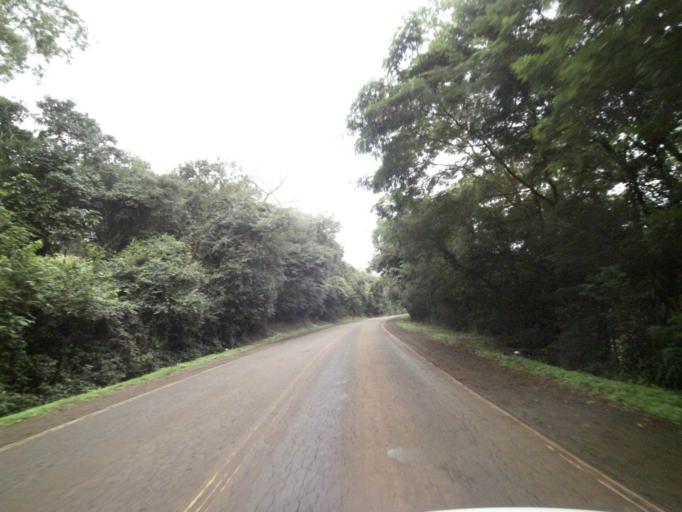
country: BR
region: Parana
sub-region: Marechal Candido Rondon
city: Marechal Candido Rondon
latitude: -24.7957
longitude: -54.2172
